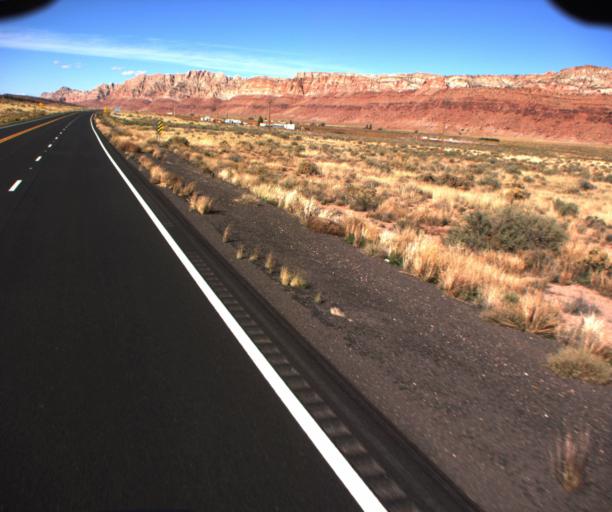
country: US
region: Arizona
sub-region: Coconino County
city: LeChee
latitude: 36.4638
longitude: -111.5672
